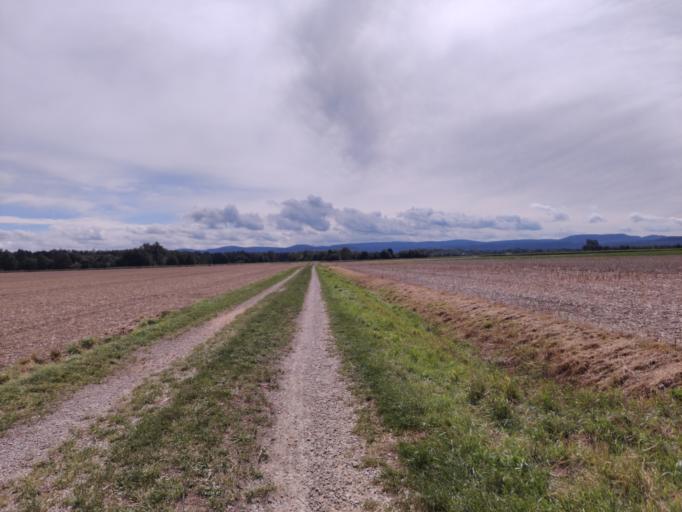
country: DE
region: Lower Saxony
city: Langelsheim
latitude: 51.9840
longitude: 10.3664
